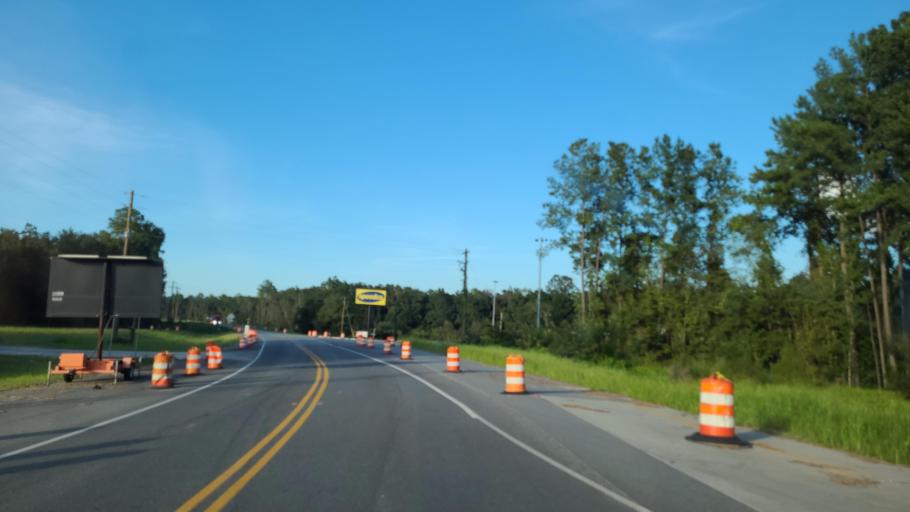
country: US
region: Georgia
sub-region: Echols County
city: Statenville
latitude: 30.6453
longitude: -83.1867
